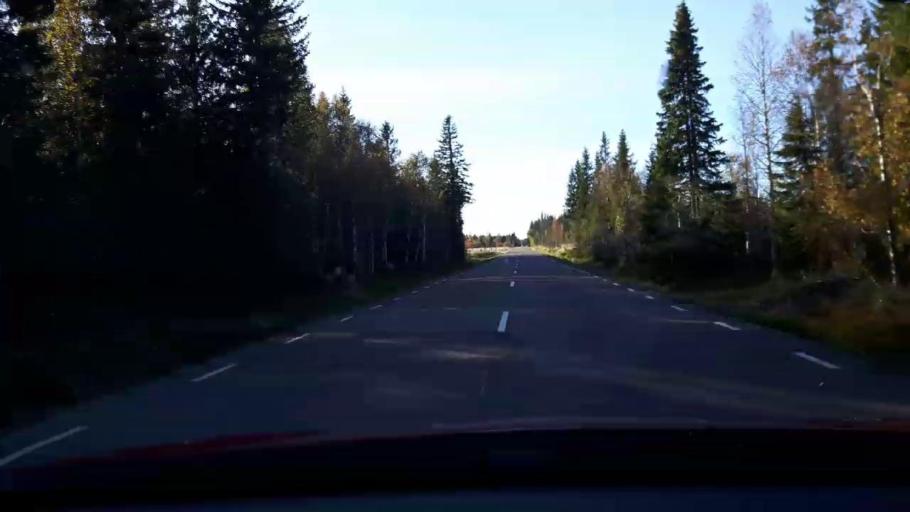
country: SE
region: Jaemtland
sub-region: Stroemsunds Kommun
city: Stroemsund
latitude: 63.8622
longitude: 15.1668
